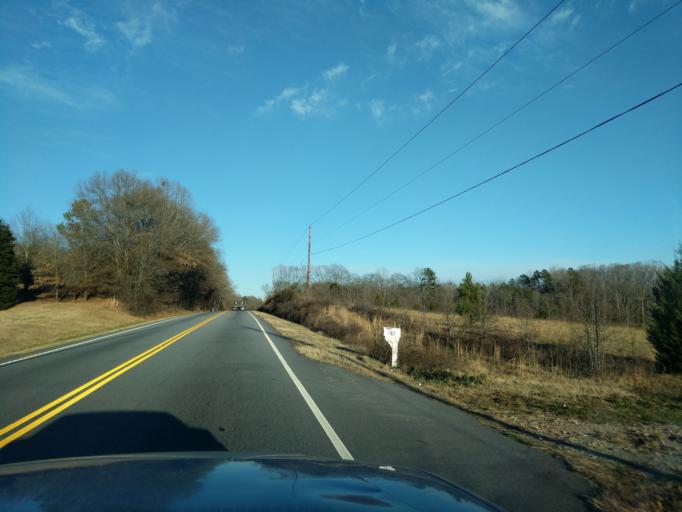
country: US
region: South Carolina
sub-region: Greenville County
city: Simpsonville
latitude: 34.6569
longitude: -82.2822
